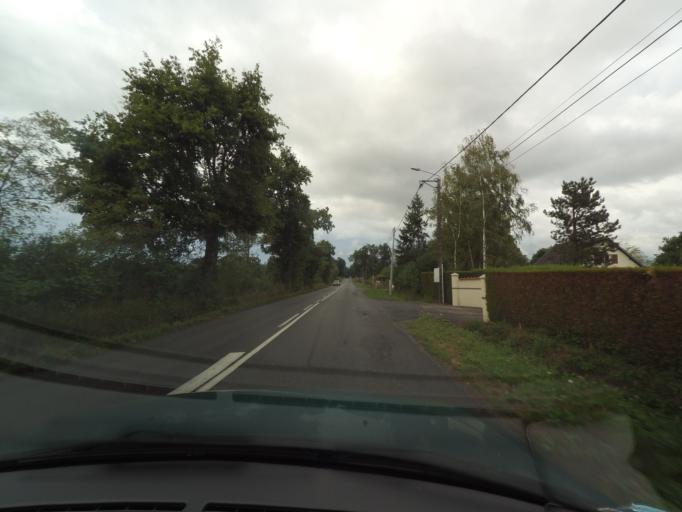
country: FR
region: Limousin
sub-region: Departement de la Haute-Vienne
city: Aixe-sur-Vienne
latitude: 45.7806
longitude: 1.1187
